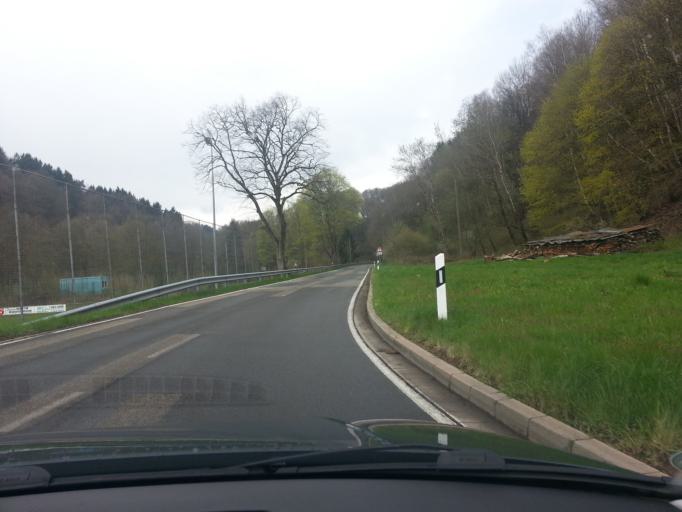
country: DE
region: Rheinland-Pfalz
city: Wiesbach
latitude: 49.3312
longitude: 7.4492
